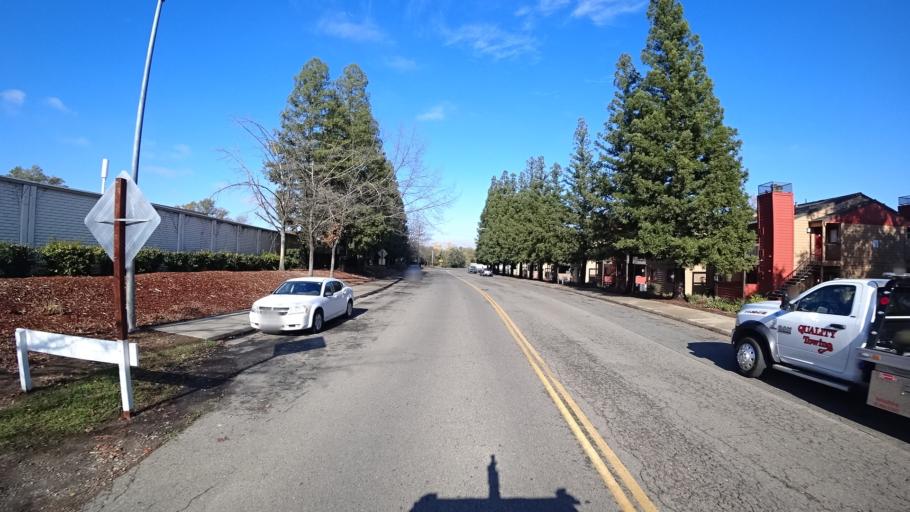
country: US
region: California
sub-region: Sacramento County
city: Foothill Farms
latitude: 38.6829
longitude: -121.3340
